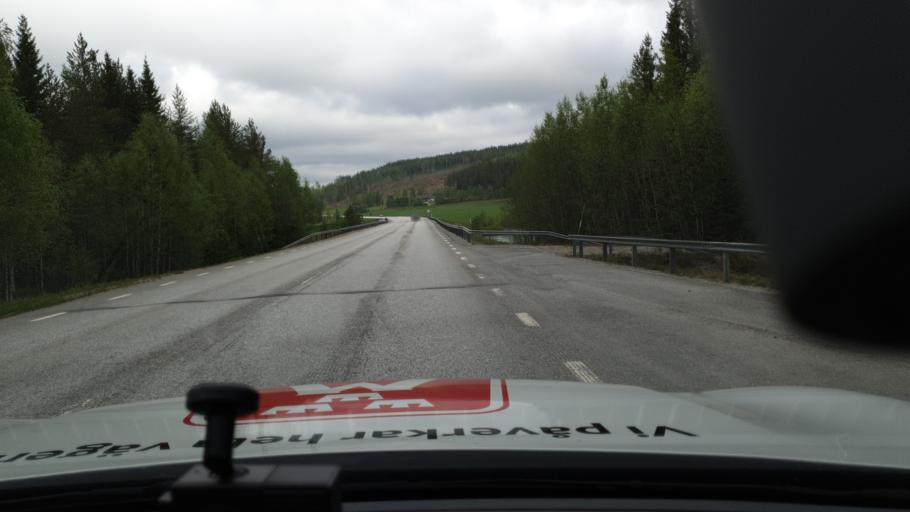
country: SE
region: Vaesterbotten
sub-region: Vannas Kommun
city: Vannasby
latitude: 64.0999
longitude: 19.9735
